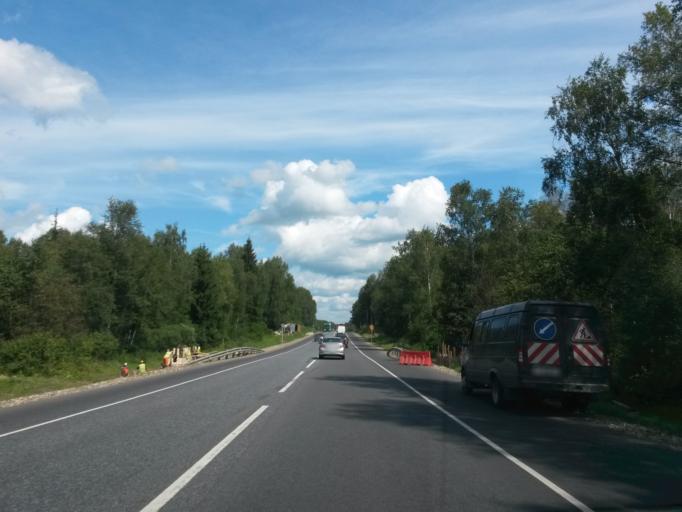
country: RU
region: Jaroslavl
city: Pereslavl'-Zalesskiy
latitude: 56.8264
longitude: 38.9107
